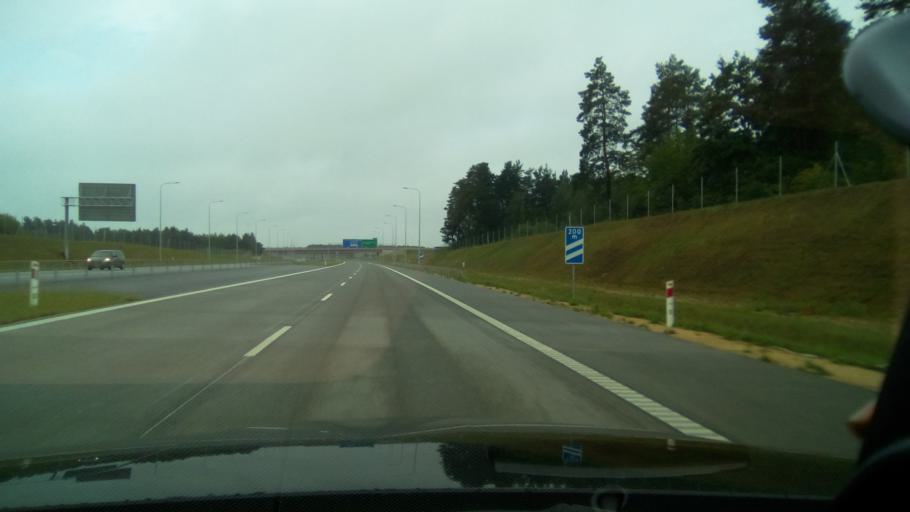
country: PL
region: Silesian Voivodeship
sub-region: Powiat klobucki
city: Kamyk
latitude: 50.8525
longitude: 19.0475
